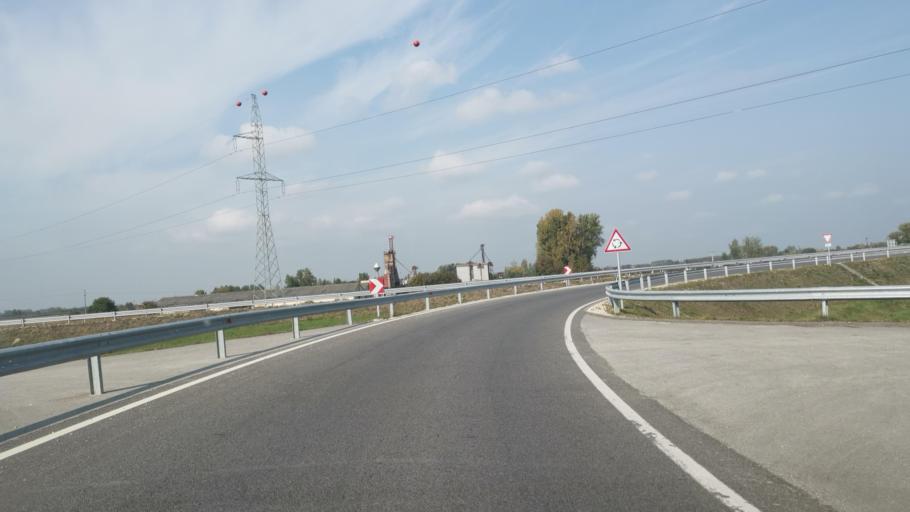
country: HU
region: Gyor-Moson-Sopron
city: Kapuvar
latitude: 47.5698
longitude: 17.0468
